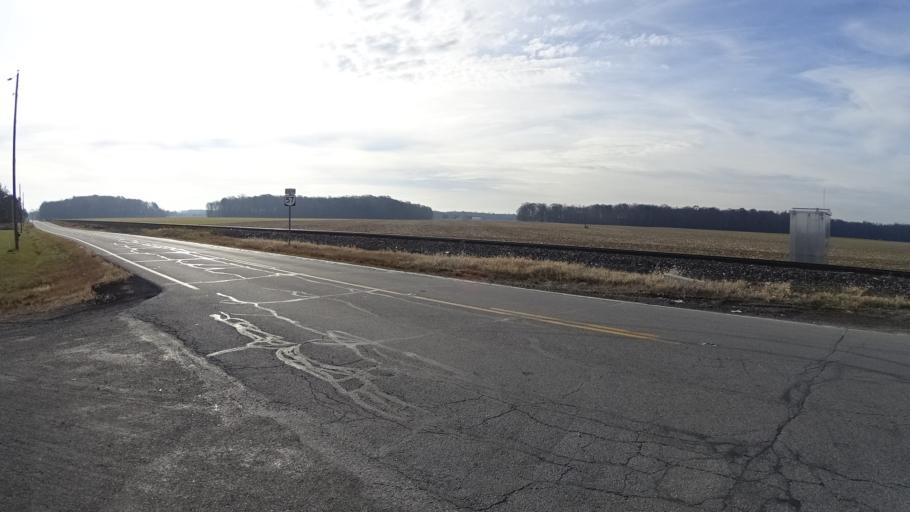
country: US
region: Ohio
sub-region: Lorain County
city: Grafton
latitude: 41.2073
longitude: -81.9836
